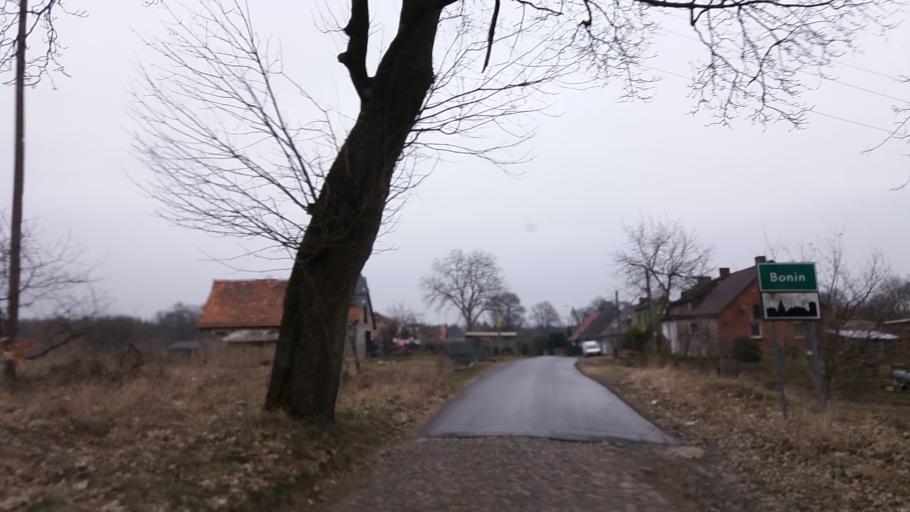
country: PL
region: West Pomeranian Voivodeship
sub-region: Powiat choszczenski
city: Choszczno
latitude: 53.1943
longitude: 15.3517
